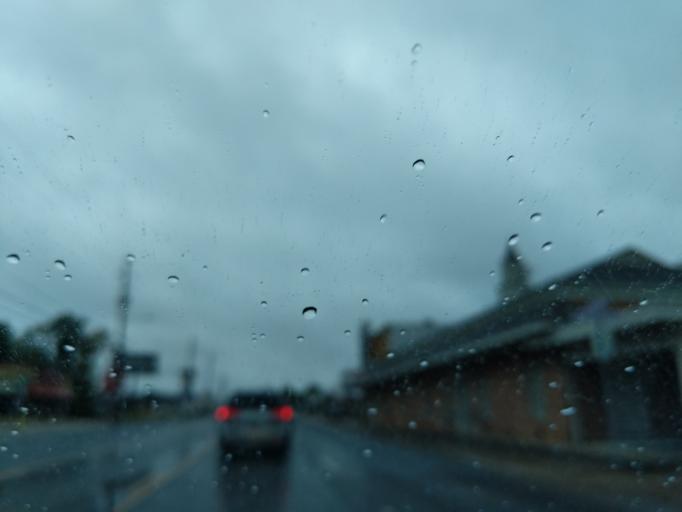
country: US
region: Texas
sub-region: Nacogdoches County
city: Nacogdoches
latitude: 31.6236
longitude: -94.6523
